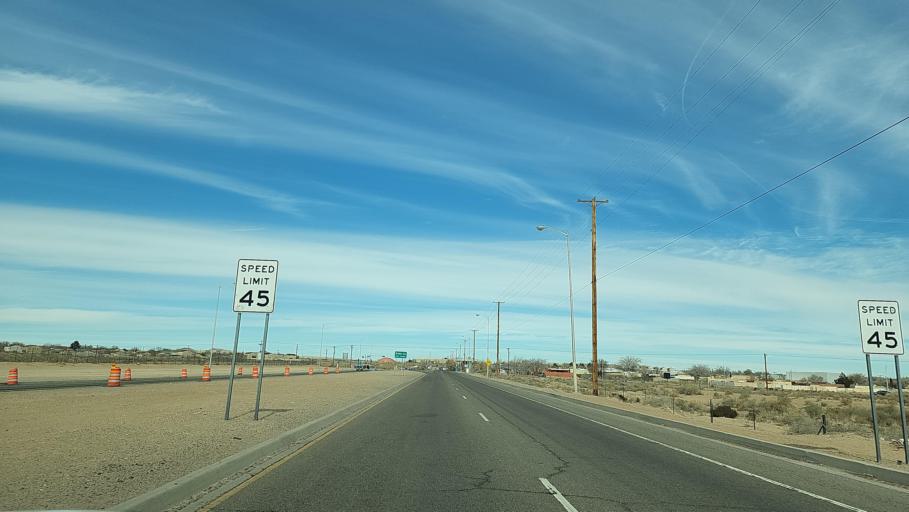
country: US
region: New Mexico
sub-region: Bernalillo County
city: Albuquerque
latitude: 35.0676
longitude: -106.7107
